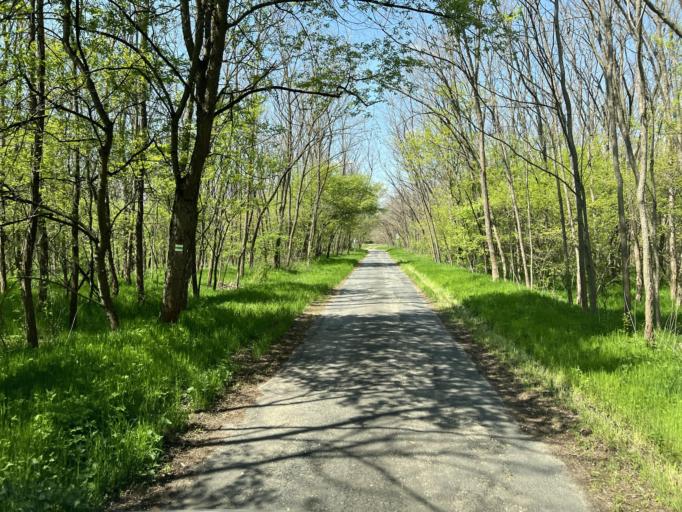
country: HU
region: Pest
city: Kakucs
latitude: 47.2720
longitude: 19.3589
